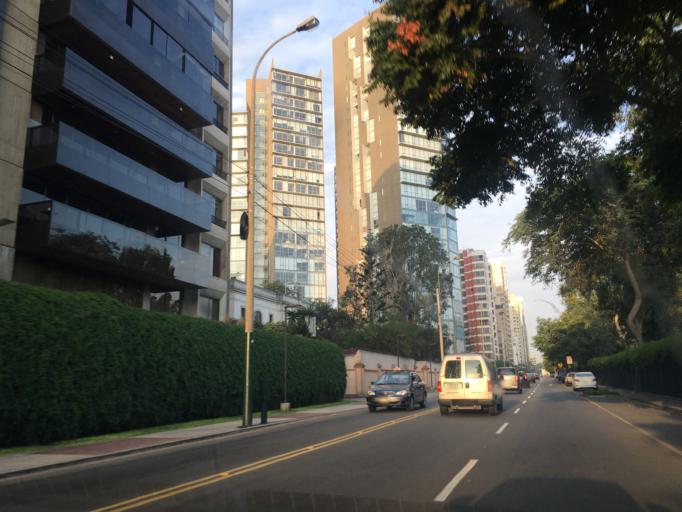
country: PE
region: Lima
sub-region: Lima
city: San Isidro
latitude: -12.0994
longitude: -77.0446
